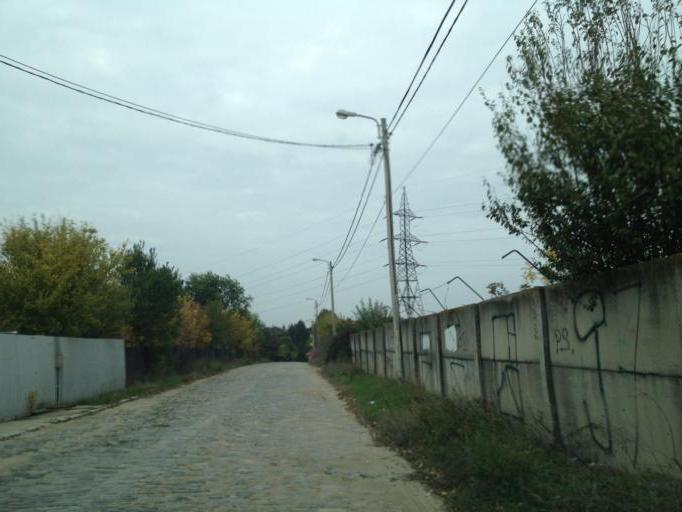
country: RO
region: Dolj
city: Craiova
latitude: 44.2936
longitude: 23.8064
